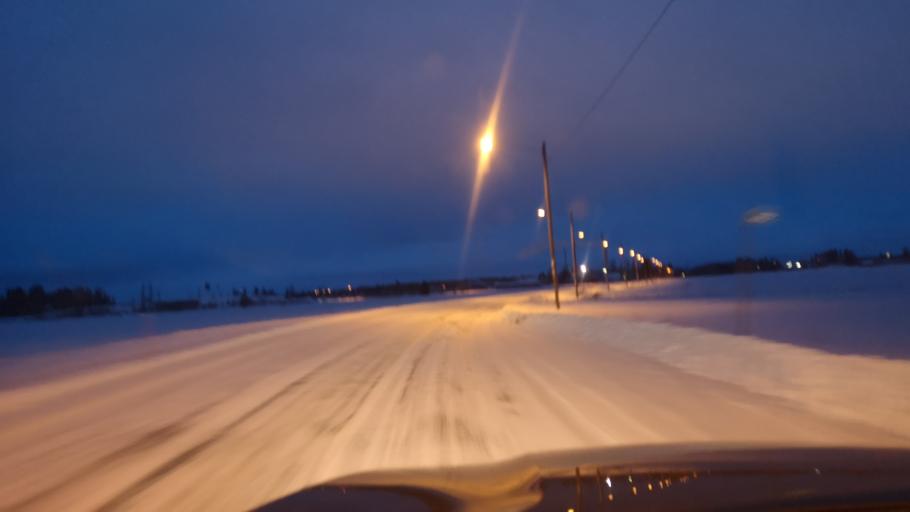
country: FI
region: Varsinais-Suomi
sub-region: Loimaa
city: Loimaa
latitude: 60.8627
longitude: 23.0802
